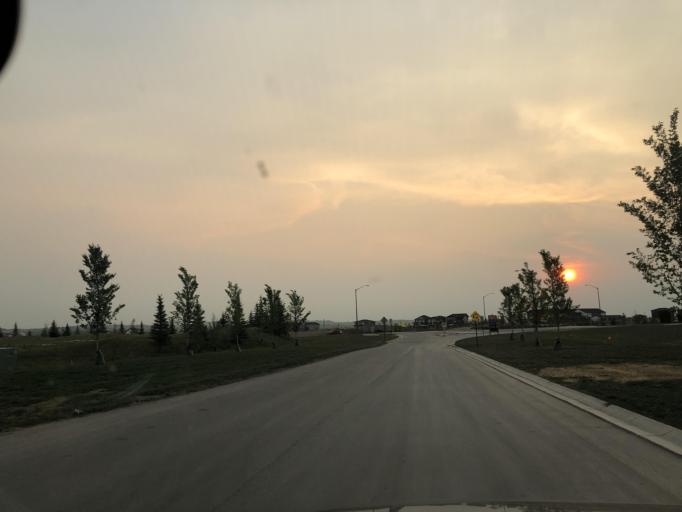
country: CA
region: Alberta
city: Cochrane
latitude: 51.1199
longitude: -114.3852
